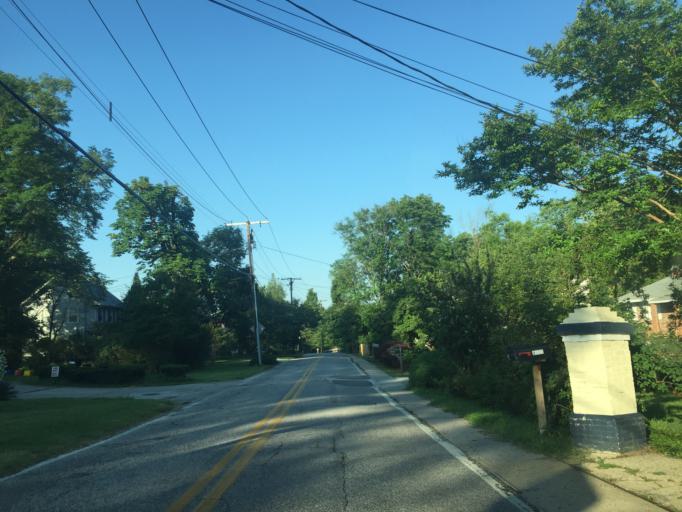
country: US
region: Maryland
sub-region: Howard County
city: Elkridge
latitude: 39.2267
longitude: -76.7070
